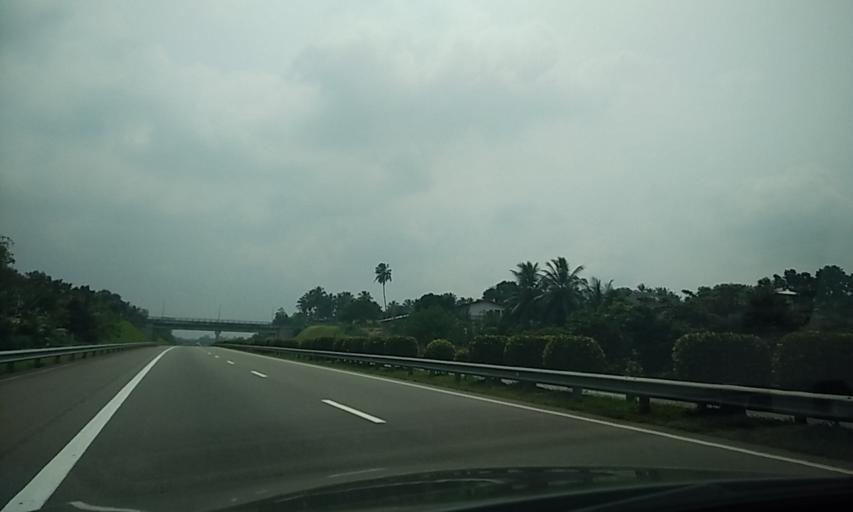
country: LK
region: Western
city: Homagama
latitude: 6.8661
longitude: 79.9783
